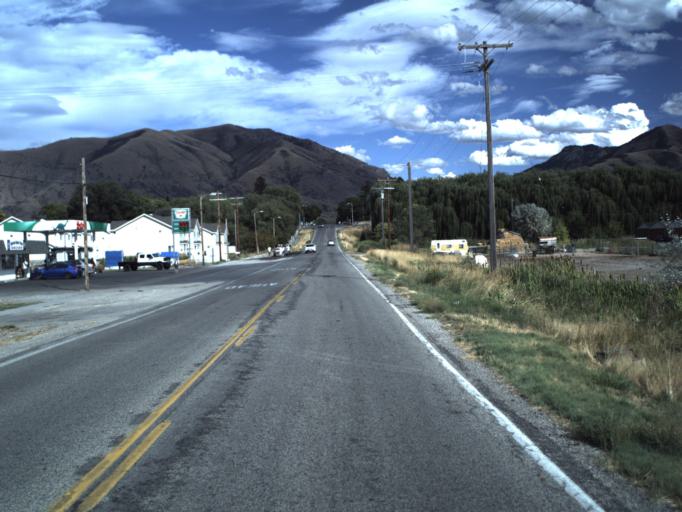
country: US
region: Utah
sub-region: Cache County
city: Hyrum
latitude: 41.6342
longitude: -111.8653
